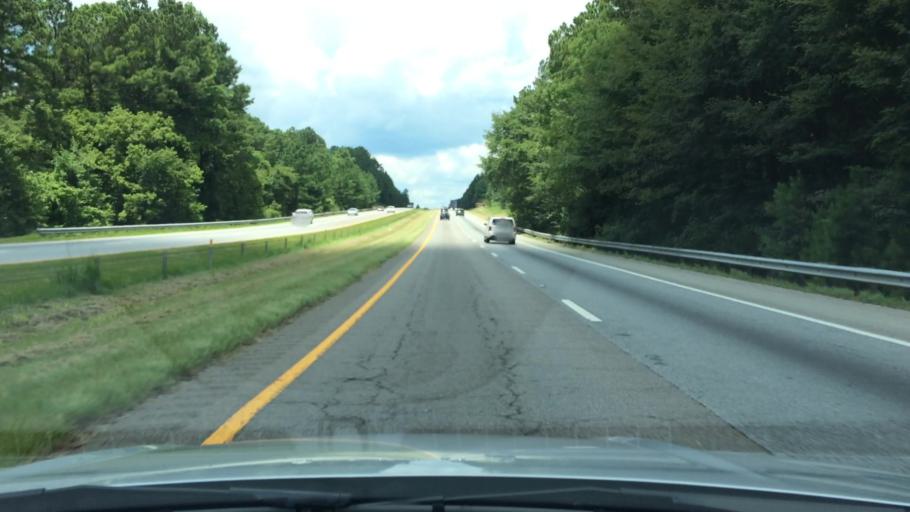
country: US
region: South Carolina
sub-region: Newberry County
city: Prosperity
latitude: 34.2765
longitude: -81.5180
